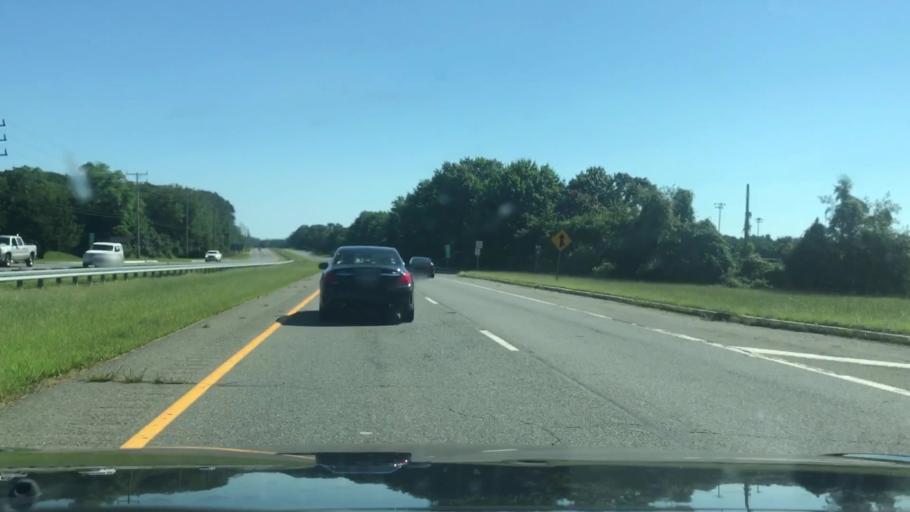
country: US
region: New Jersey
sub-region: Monmouth County
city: Shark River Hills
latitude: 40.1714
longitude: -74.0625
